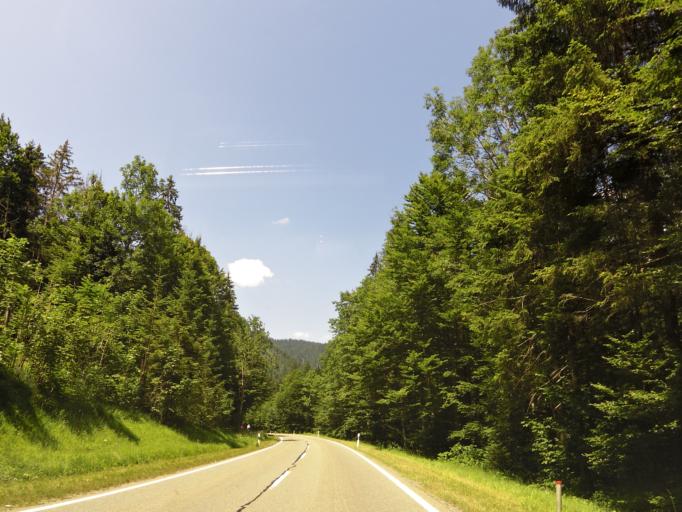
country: DE
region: Bavaria
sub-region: Upper Bavaria
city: Reit im Winkl
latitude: 47.6722
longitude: 12.5469
